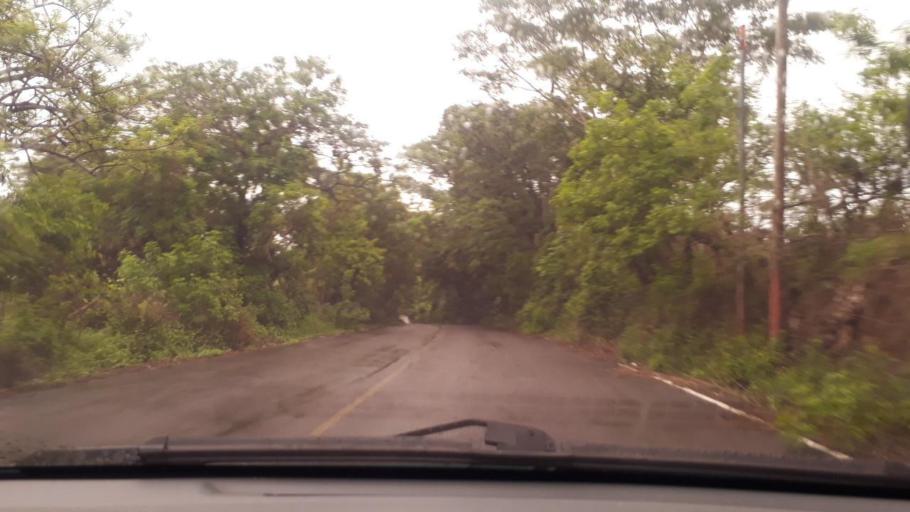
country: GT
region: Jutiapa
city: Comapa
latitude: 14.0432
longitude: -89.9195
